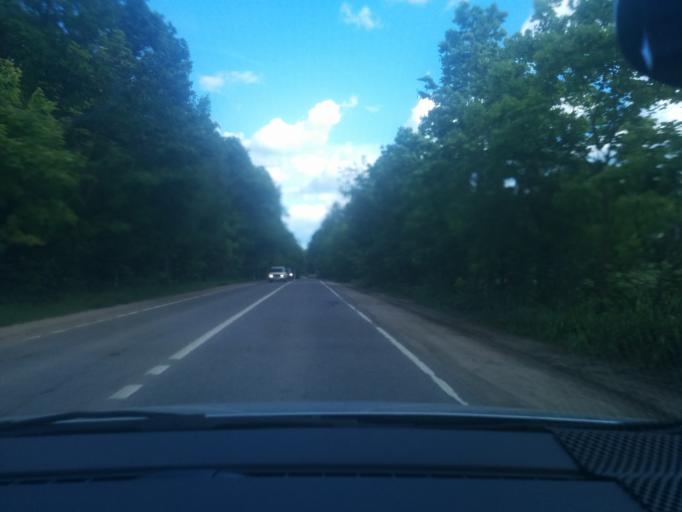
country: RU
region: Moskovskaya
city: Lugovaya
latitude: 56.0505
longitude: 37.4877
